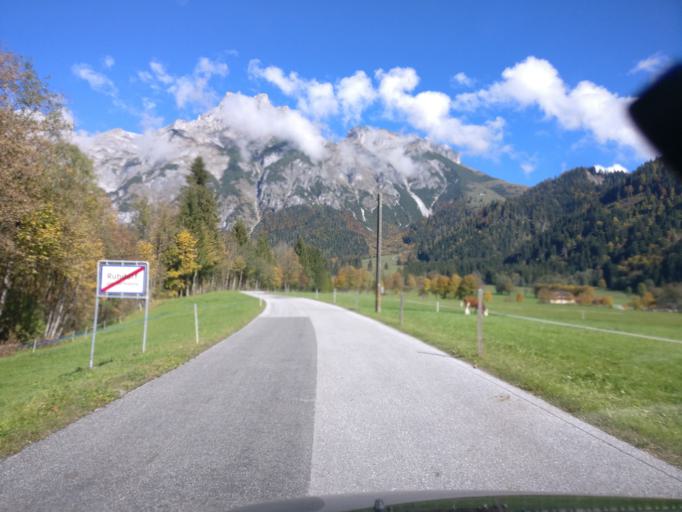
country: AT
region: Salzburg
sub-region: Politischer Bezirk Sankt Johann im Pongau
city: Werfenweng
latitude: 47.4702
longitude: 13.2649
